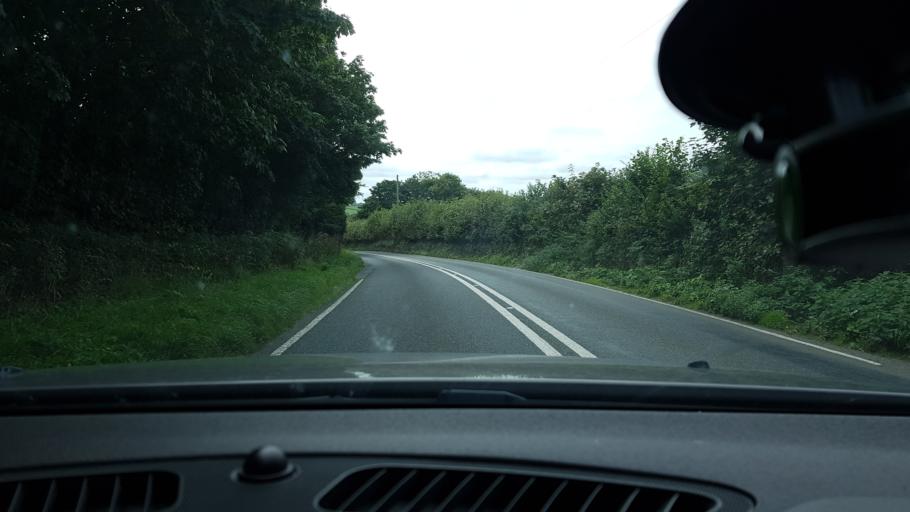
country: GB
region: England
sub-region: Cornwall
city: Camelford
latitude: 50.5967
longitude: -4.7146
